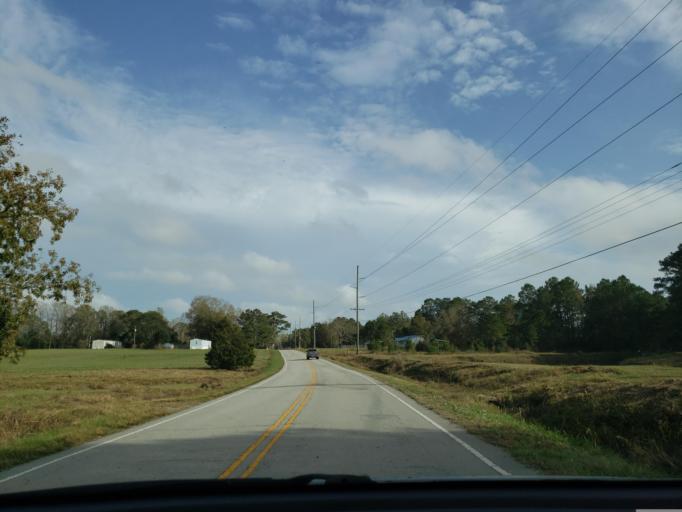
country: US
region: North Carolina
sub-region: Onslow County
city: Jacksonville
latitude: 34.6890
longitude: -77.5388
